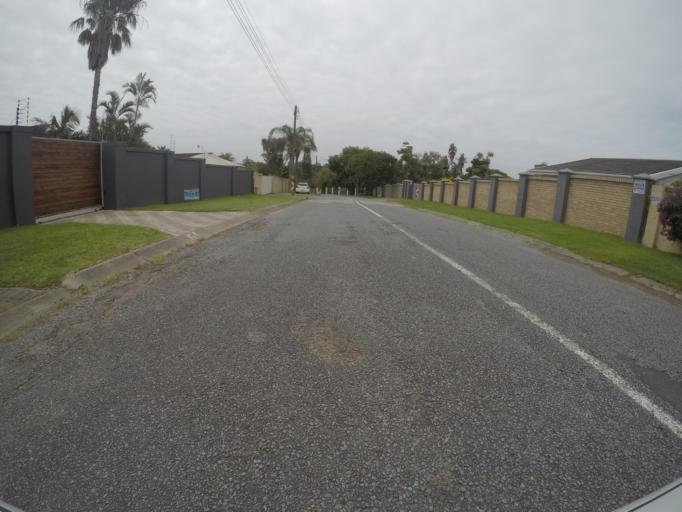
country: ZA
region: Eastern Cape
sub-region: Buffalo City Metropolitan Municipality
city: East London
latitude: -32.9753
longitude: 27.9426
